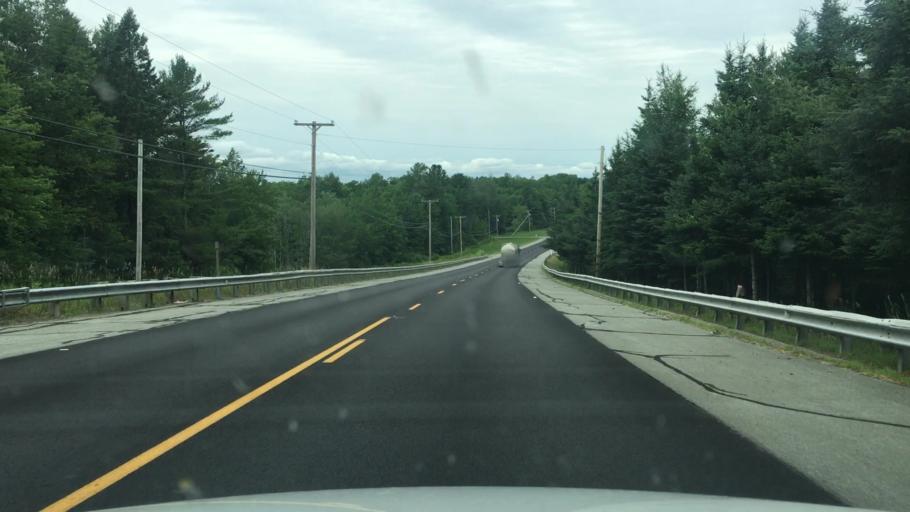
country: US
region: Maine
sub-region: Waldo County
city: Palermo
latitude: 44.3836
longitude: -69.4620
